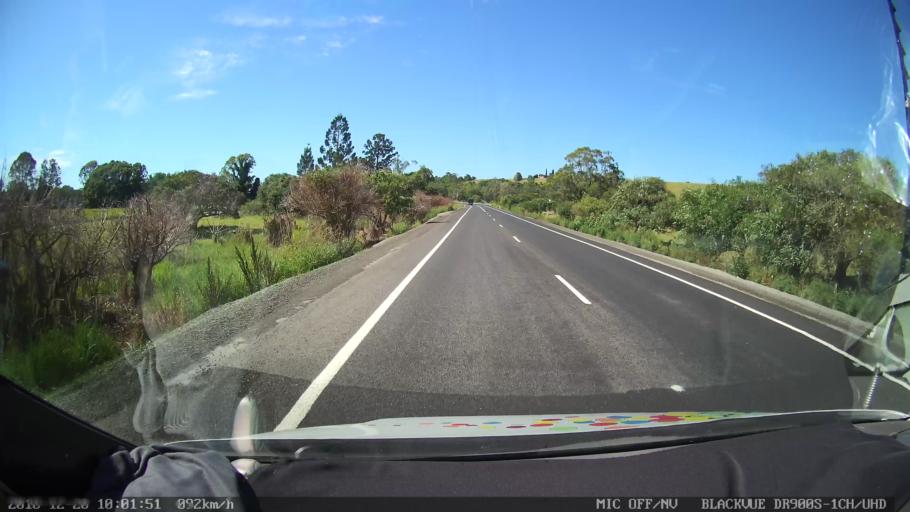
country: AU
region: New South Wales
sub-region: Lismore Municipality
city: Lismore
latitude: -28.8501
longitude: 153.2613
